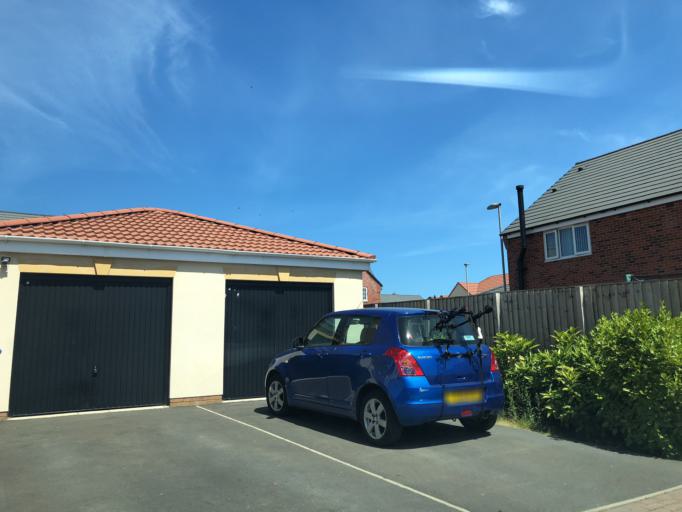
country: GB
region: England
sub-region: North Yorkshire
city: Scarborough
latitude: 54.2465
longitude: -0.3873
